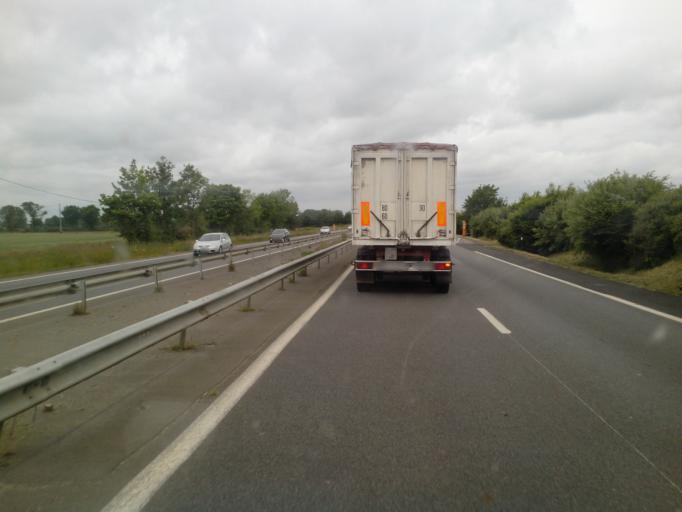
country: FR
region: Brittany
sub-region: Departement des Cotes-d'Armor
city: Plestan
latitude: 48.4115
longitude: -2.4264
